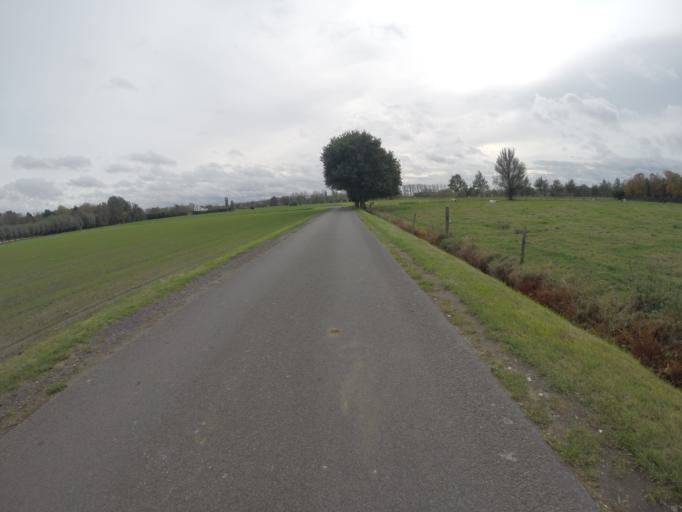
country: BE
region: Flanders
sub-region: Provincie Oost-Vlaanderen
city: Maldegem
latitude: 51.1882
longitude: 3.4329
